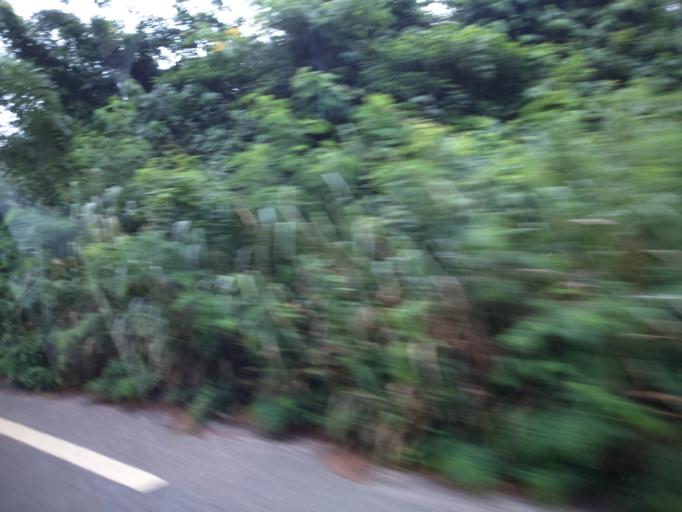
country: CI
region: Moyen-Comoe
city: Abengourou
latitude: 6.6565
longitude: -3.2858
